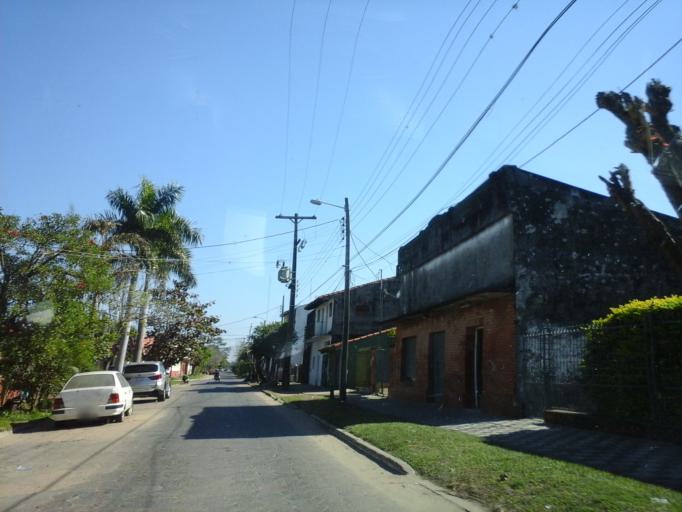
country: PY
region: Neembucu
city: Pilar
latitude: -26.8611
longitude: -58.3016
